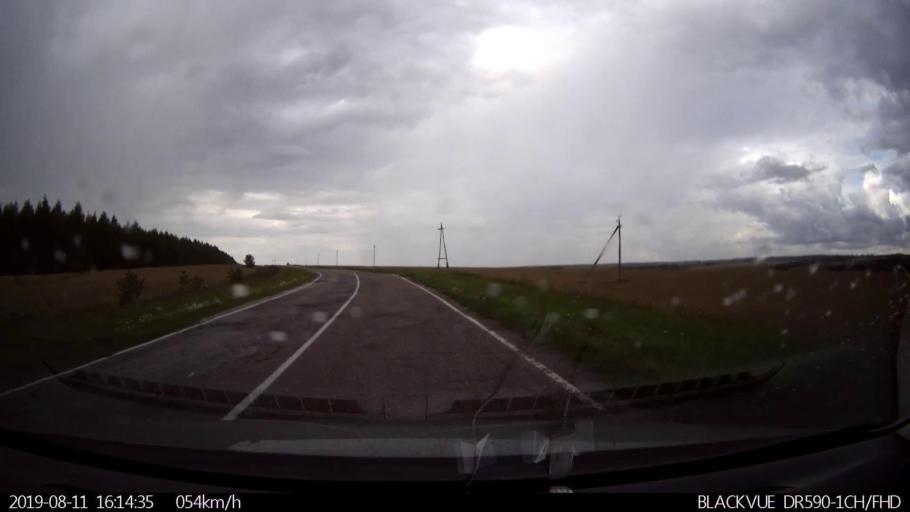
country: RU
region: Ulyanovsk
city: Mayna
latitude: 54.0307
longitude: 47.6321
